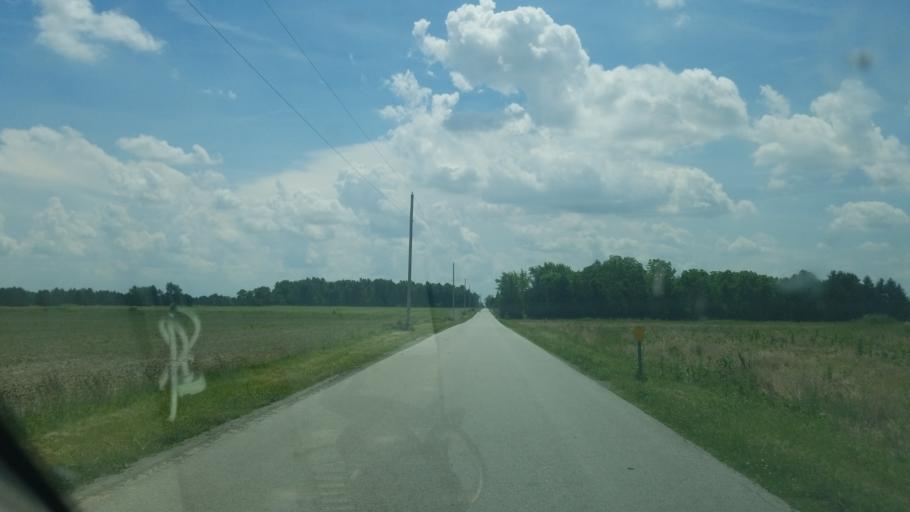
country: US
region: Ohio
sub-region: Hancock County
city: Arlington
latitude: 40.8838
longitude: -83.5996
